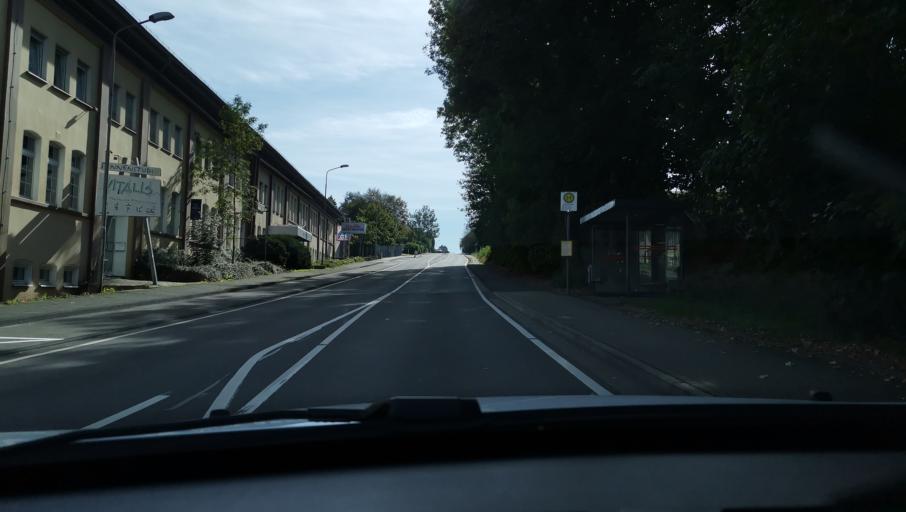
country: DE
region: North Rhine-Westphalia
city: Kierspe
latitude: 51.1319
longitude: 7.5899
